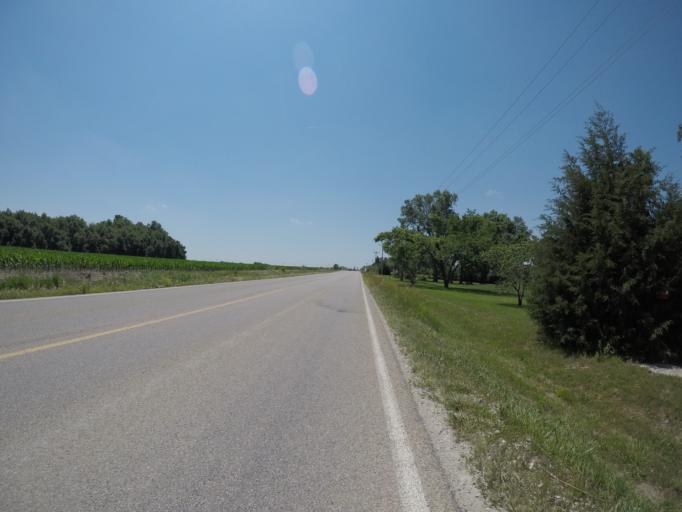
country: US
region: Kansas
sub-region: Riley County
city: Manhattan
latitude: 39.2371
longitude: -96.4454
